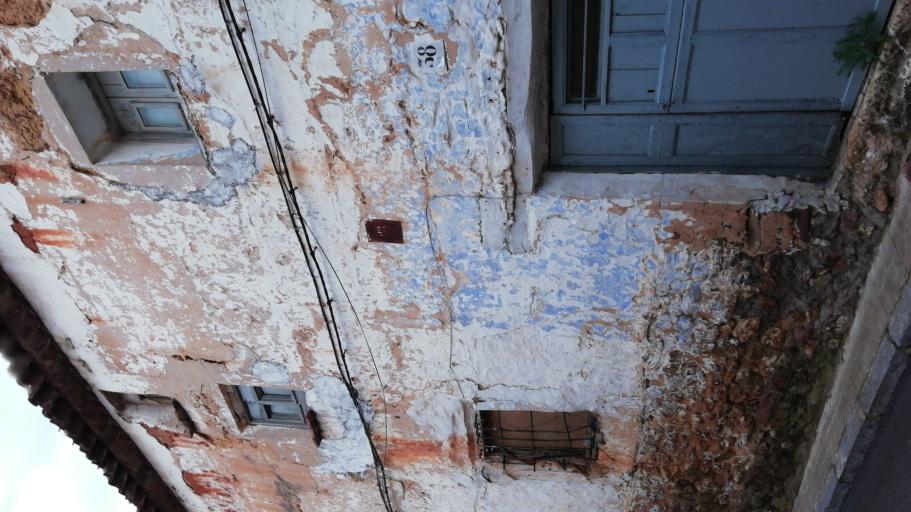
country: ES
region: Castille and Leon
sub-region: Provincia de Soria
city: Olvega
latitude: 41.7790
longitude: -1.9821
